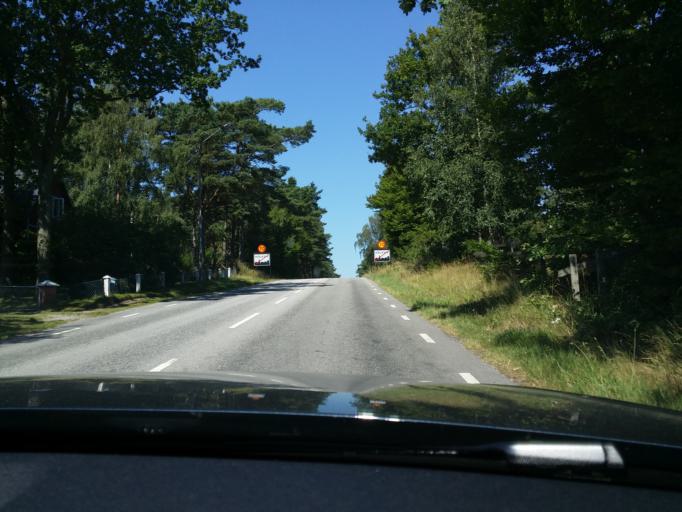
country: SE
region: Blekinge
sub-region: Solvesborgs Kommun
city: Soelvesborg
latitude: 56.0147
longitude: 14.6886
